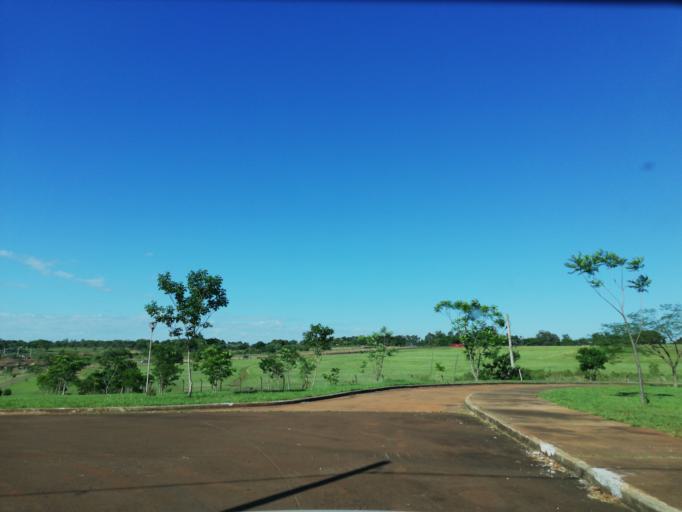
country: AR
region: Misiones
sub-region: Departamento de Capital
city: Posadas
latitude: -27.3959
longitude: -55.9659
